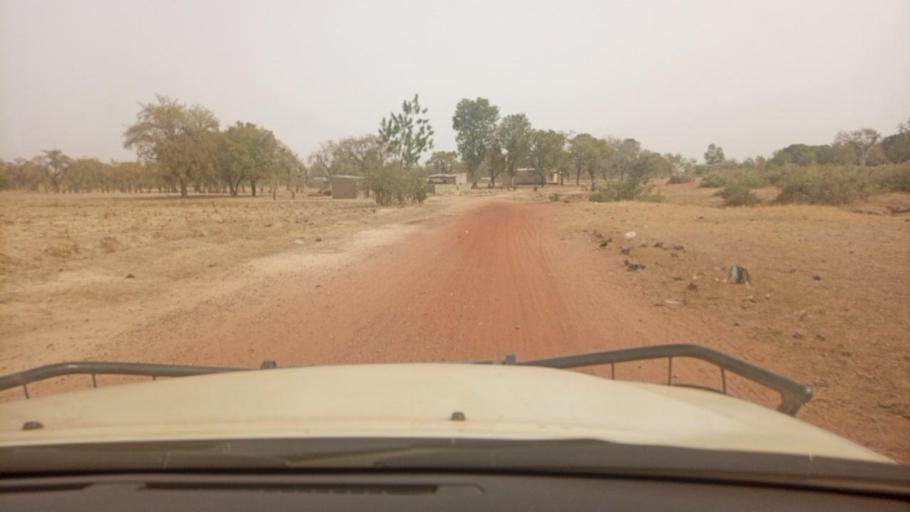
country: BF
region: Boucle du Mouhoun
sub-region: Province des Banwa
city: Salanso
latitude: 12.1120
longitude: -4.3370
